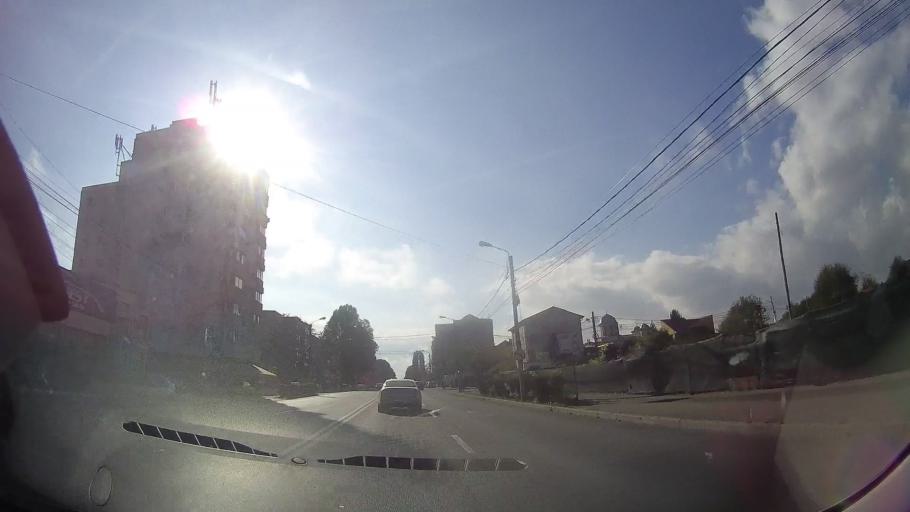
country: RO
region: Constanta
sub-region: Municipiul Constanta
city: Constanta
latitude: 44.1423
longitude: 28.6228
